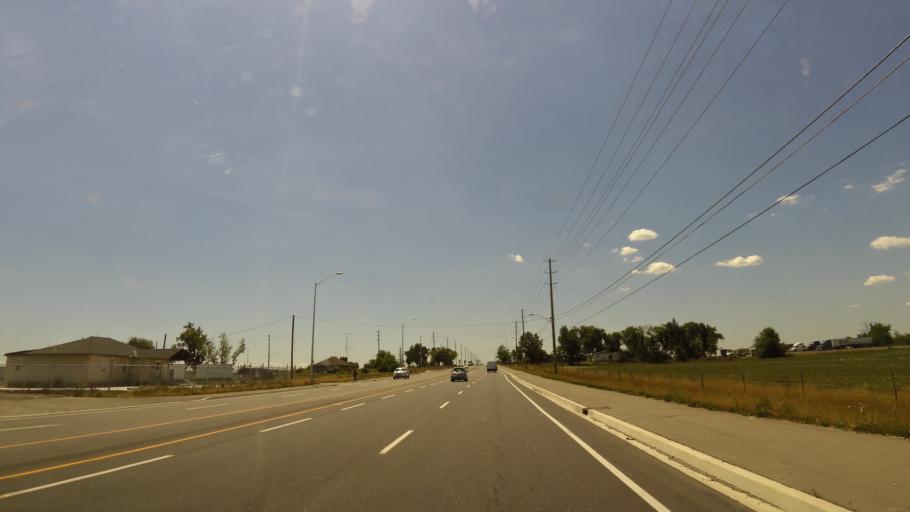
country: CA
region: Ontario
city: Brampton
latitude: 43.6045
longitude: -79.8015
